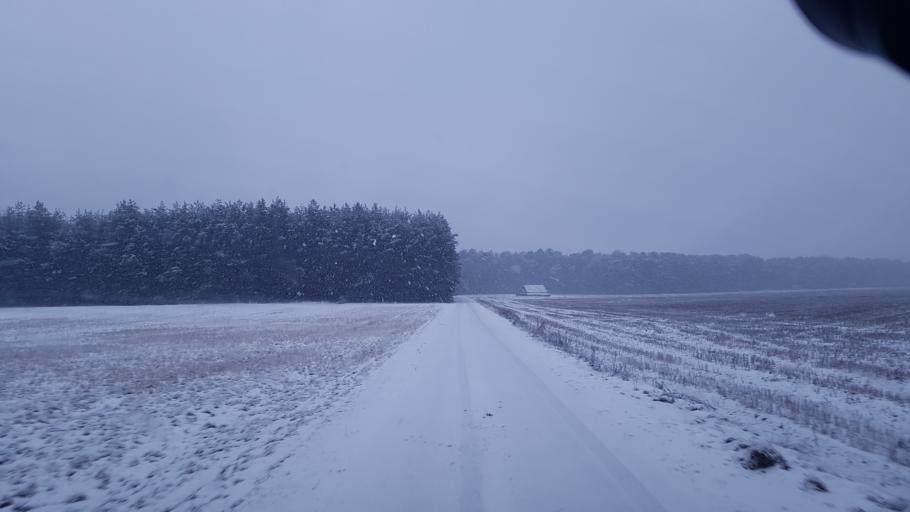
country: DE
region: Brandenburg
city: Janschwalde
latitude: 51.9050
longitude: 14.5396
